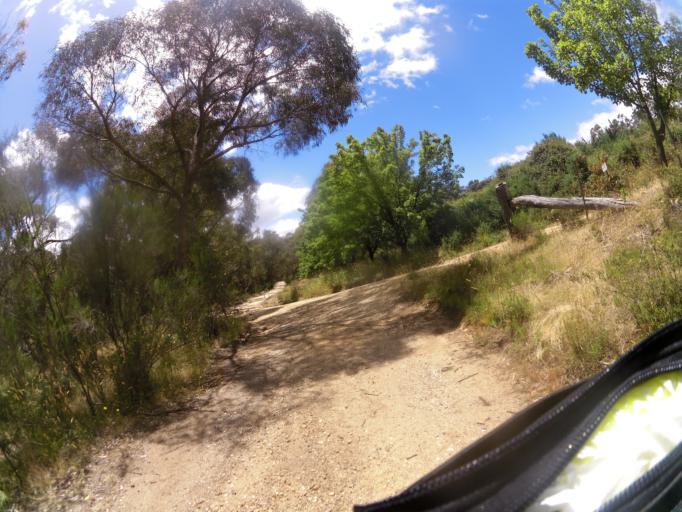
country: AU
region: Victoria
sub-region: Mount Alexander
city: Castlemaine
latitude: -37.0596
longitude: 144.2679
